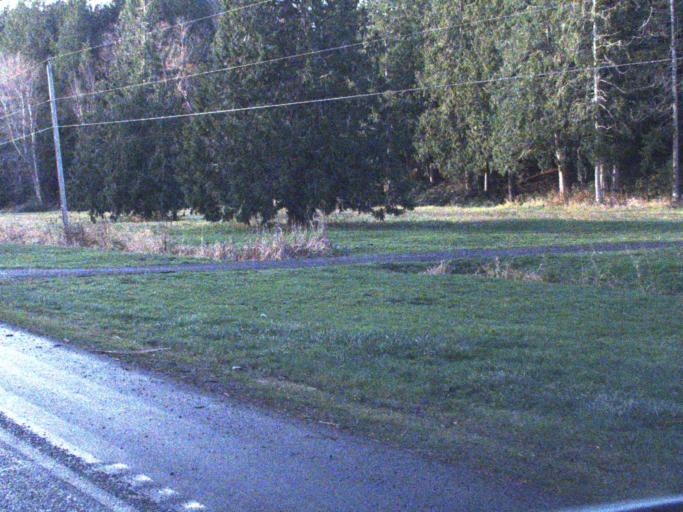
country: US
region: Washington
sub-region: Skagit County
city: Sedro-Woolley
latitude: 48.5282
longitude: -122.1692
